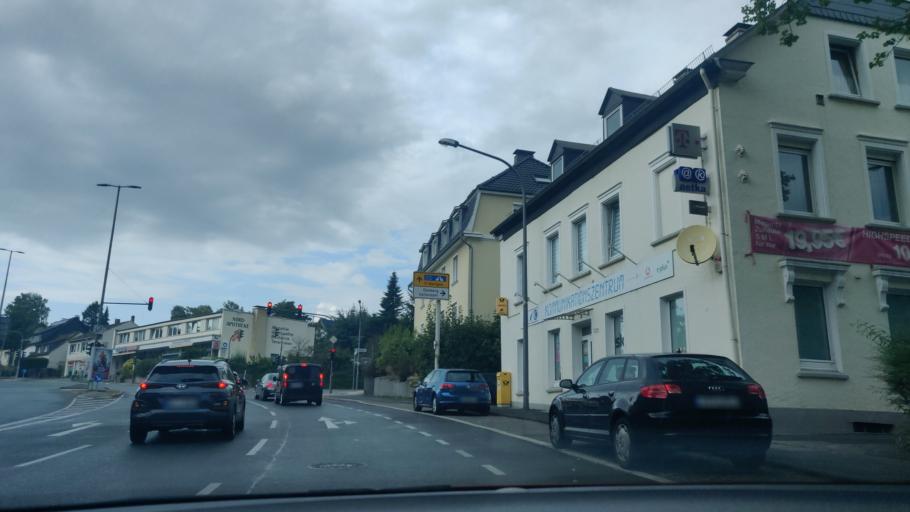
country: DE
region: North Rhine-Westphalia
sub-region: Regierungsbezirk Dusseldorf
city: Wuppertal
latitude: 51.2805
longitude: 7.1246
